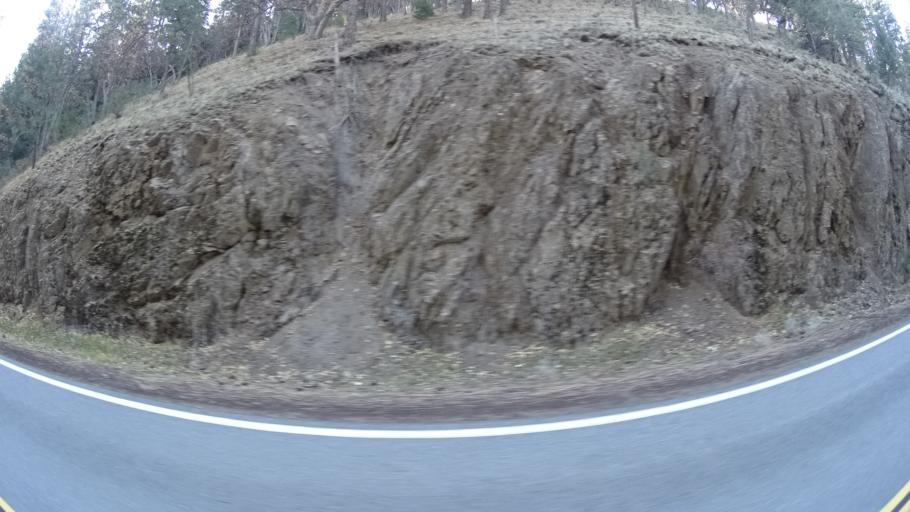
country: US
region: California
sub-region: Siskiyou County
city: Weed
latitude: 41.4658
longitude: -122.6048
